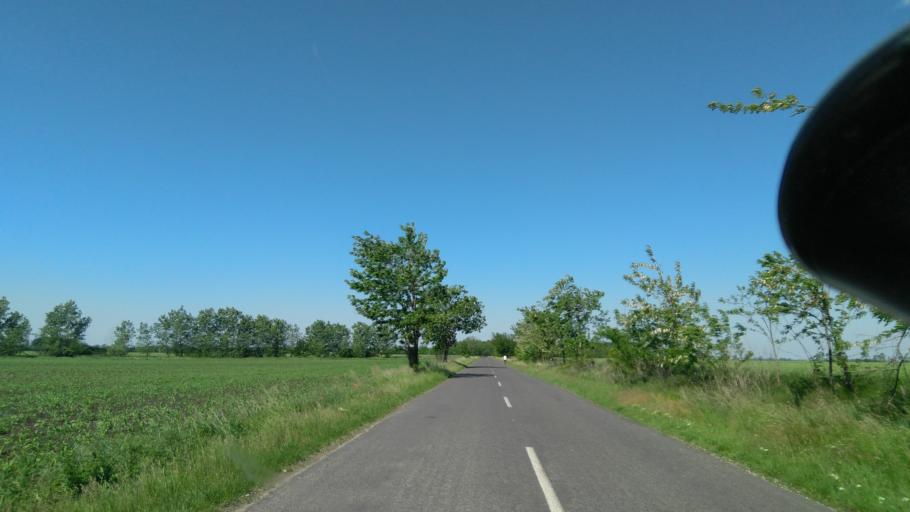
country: HU
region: Bekes
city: Kevermes
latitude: 46.4251
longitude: 21.1375
